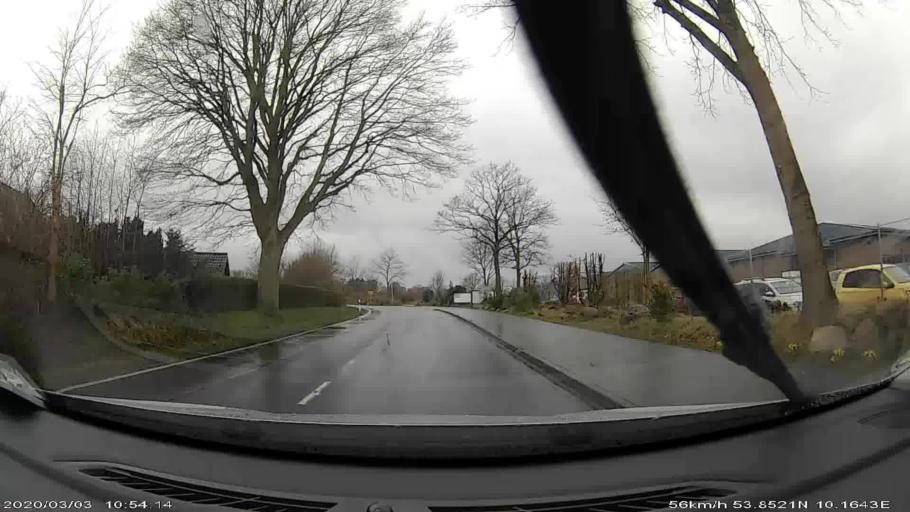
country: DE
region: Schleswig-Holstein
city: Seth
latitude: 53.8508
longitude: 10.1602
